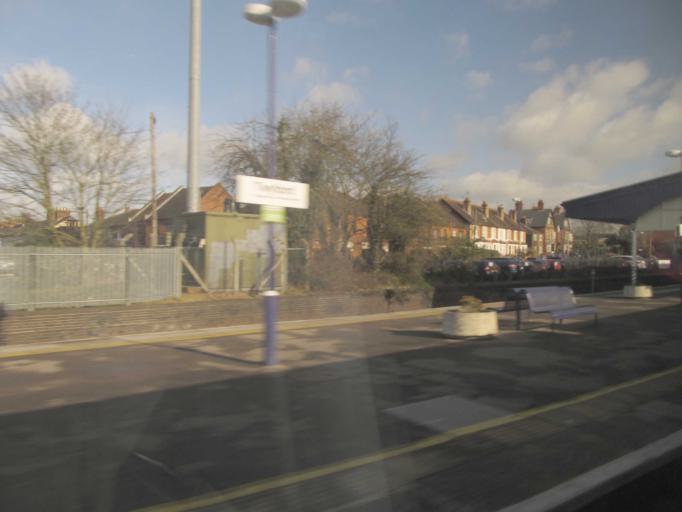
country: GB
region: England
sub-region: Wokingham
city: Twyford
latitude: 51.4755
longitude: -0.8638
